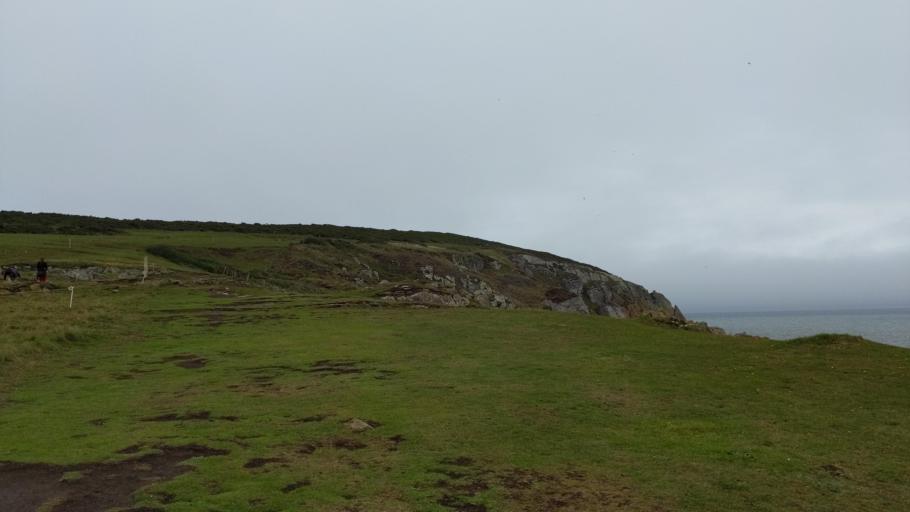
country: IE
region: Leinster
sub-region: Lu
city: Clogherhead
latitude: 53.7915
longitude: -6.2222
